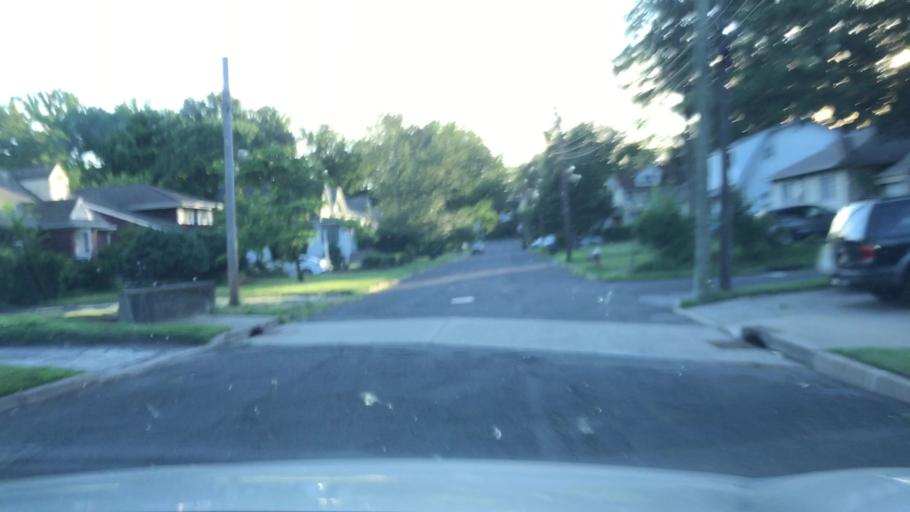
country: US
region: New Jersey
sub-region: Bergen County
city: Bergenfield
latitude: 40.9274
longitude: -73.9884
